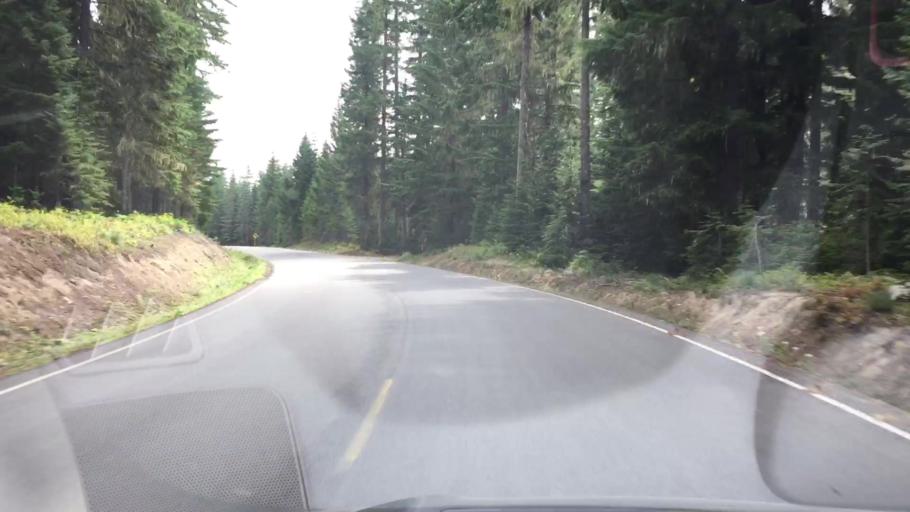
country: US
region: Washington
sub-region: Klickitat County
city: White Salmon
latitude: 46.1916
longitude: -121.6497
